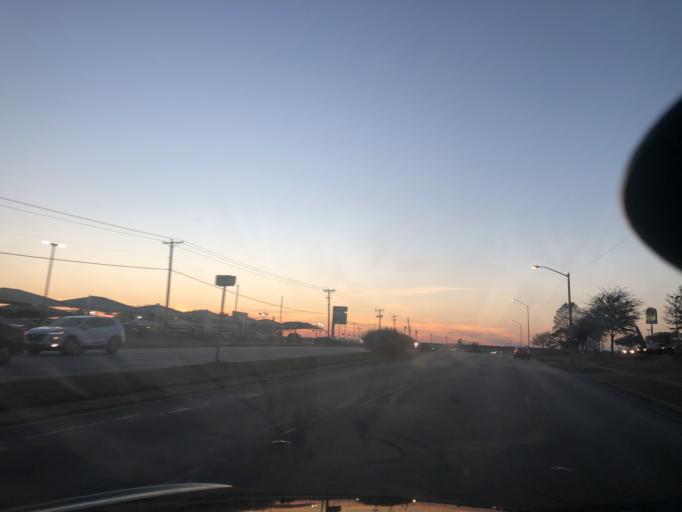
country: US
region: Texas
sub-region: Tarrant County
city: White Settlement
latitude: 32.7245
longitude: -97.4761
